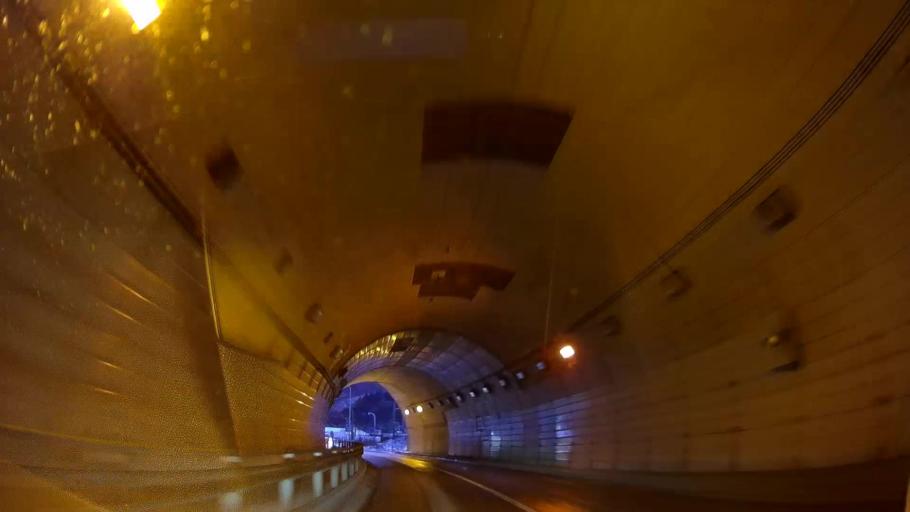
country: JP
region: Hokkaido
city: Hakodate
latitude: 41.8926
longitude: 141.0247
